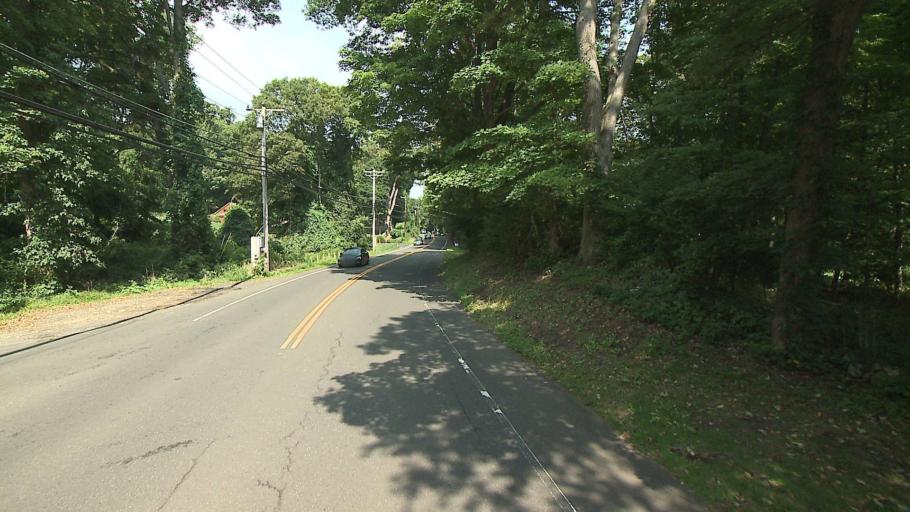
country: US
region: Connecticut
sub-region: Fairfield County
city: Ridgefield
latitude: 41.3005
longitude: -73.5061
